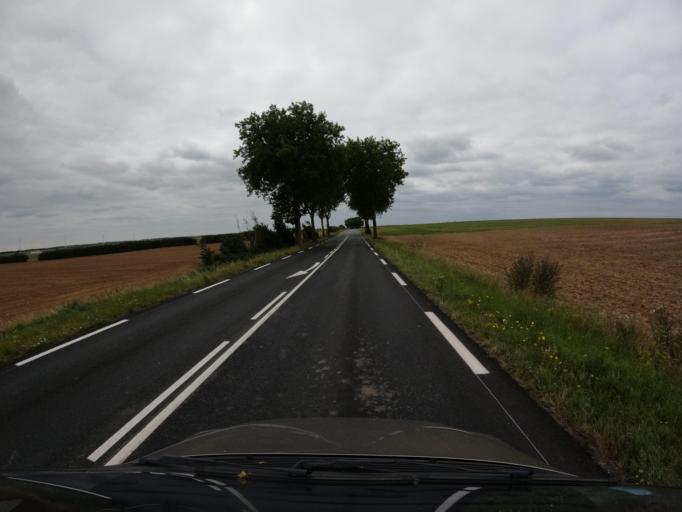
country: FR
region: Pays de la Loire
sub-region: Departement de la Vendee
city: Saint-Martin-sous-Mouzeuil
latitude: 46.5176
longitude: -0.9758
